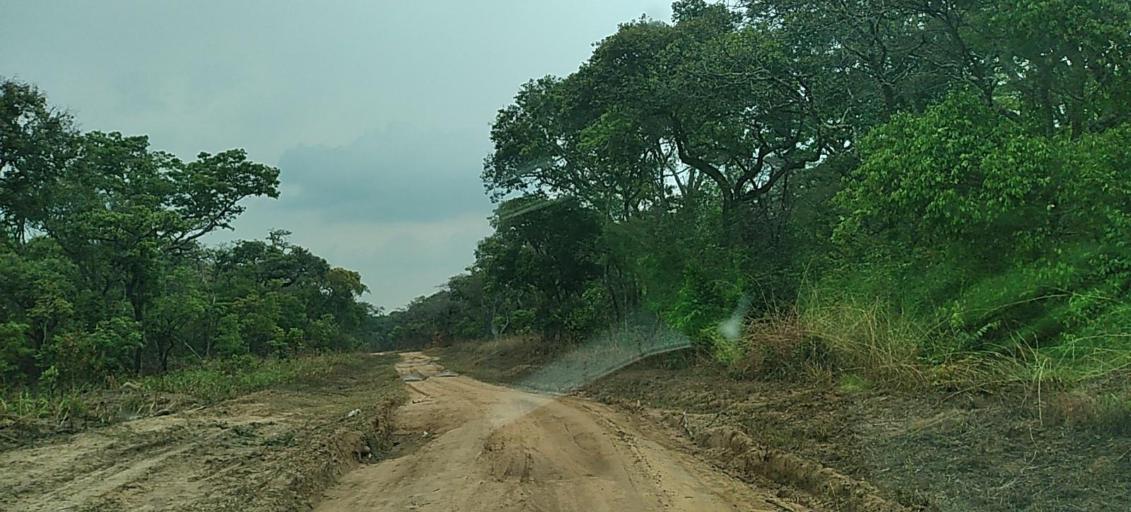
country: ZM
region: North-Western
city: Mwinilunga
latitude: -11.4695
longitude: 24.4639
